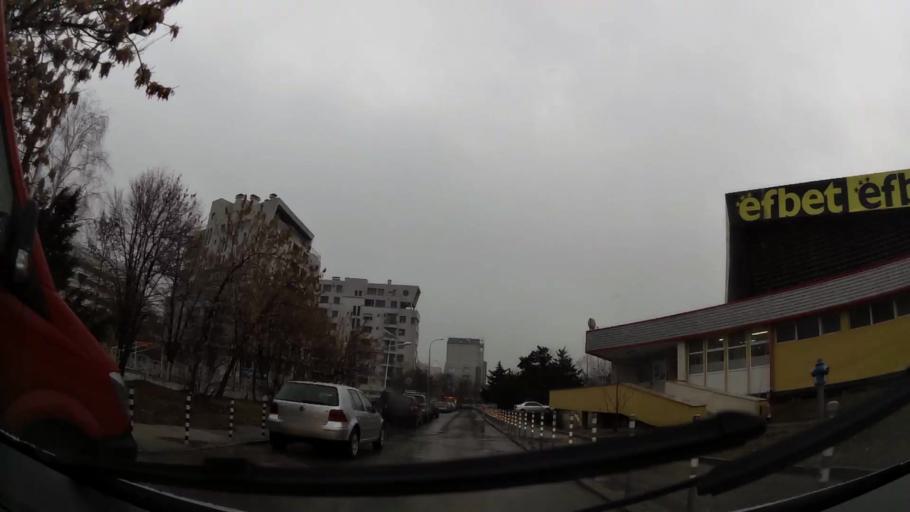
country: BG
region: Sofia-Capital
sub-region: Stolichna Obshtina
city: Sofia
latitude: 42.6519
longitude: 23.3398
